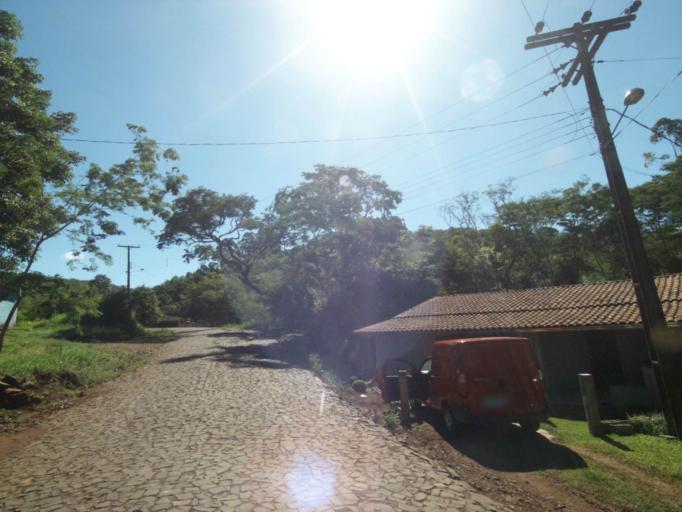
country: BR
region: Parana
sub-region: Ampere
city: Ampere
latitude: -26.1681
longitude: -53.3676
